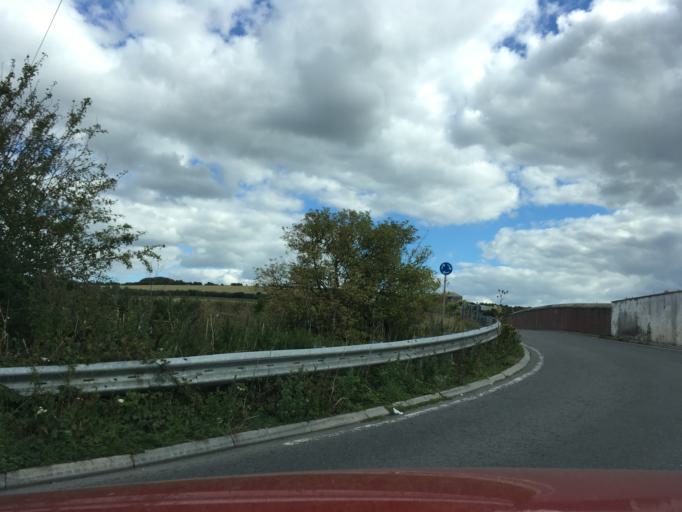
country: GB
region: England
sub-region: Wiltshire
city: Salisbury
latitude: 51.0960
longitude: -1.7606
